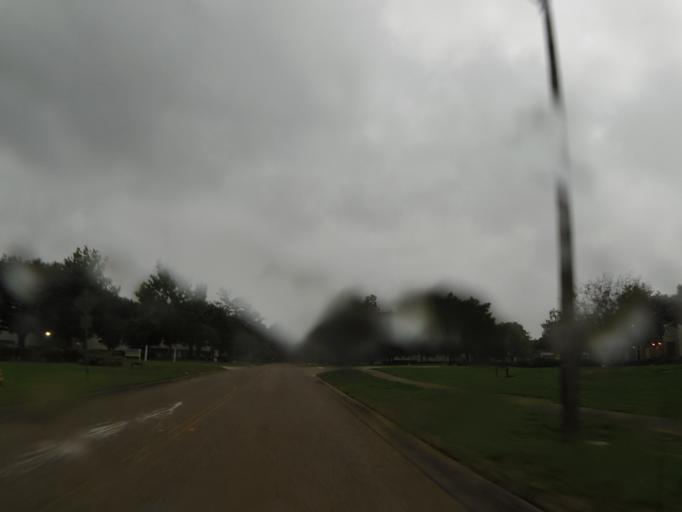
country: US
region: Florida
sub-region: Duval County
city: Neptune Beach
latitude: 30.2823
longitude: -81.5154
